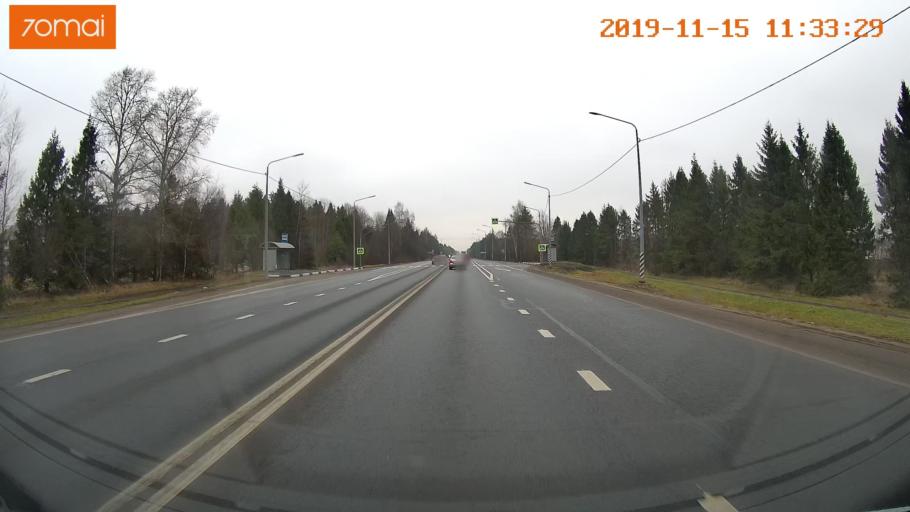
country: RU
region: Vologda
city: Molochnoye
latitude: 59.1894
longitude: 39.5927
